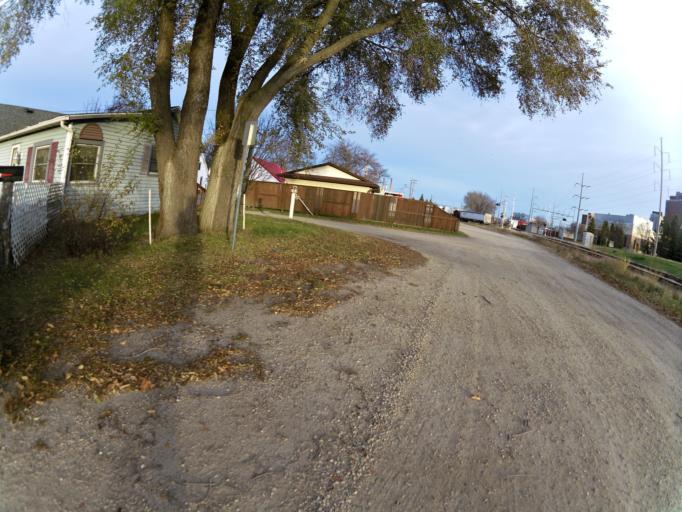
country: US
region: Minnesota
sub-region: Olmsted County
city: Rochester
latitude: 44.0283
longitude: -92.4692
